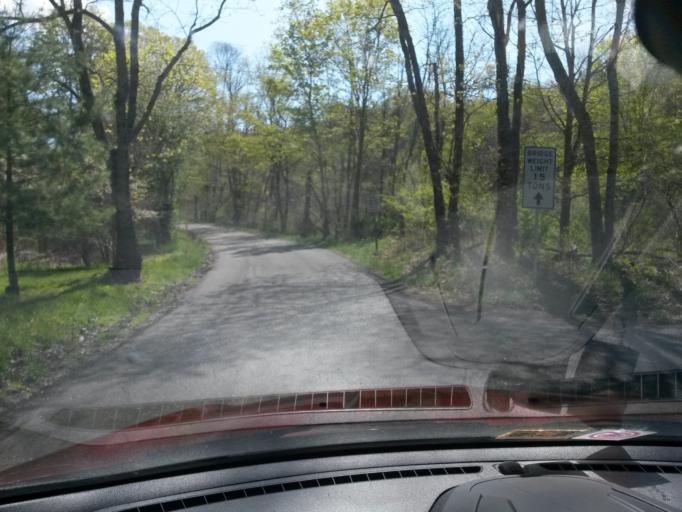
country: US
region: Virginia
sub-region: Bath County
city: Warm Springs
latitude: 38.2168
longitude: -79.6766
